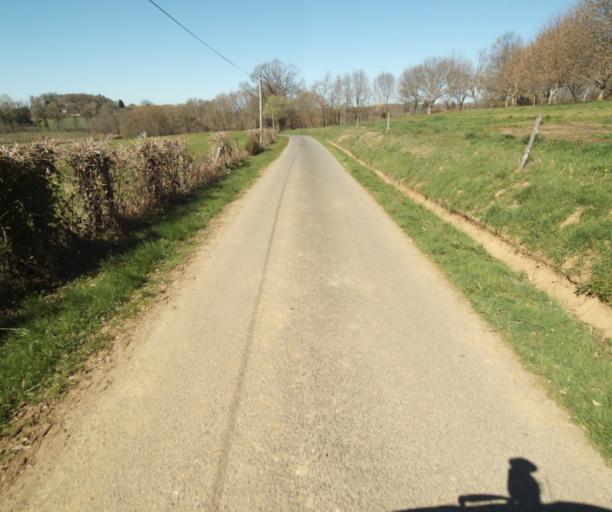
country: FR
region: Limousin
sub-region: Departement de la Correze
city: Saint-Clement
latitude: 45.3907
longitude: 1.6503
